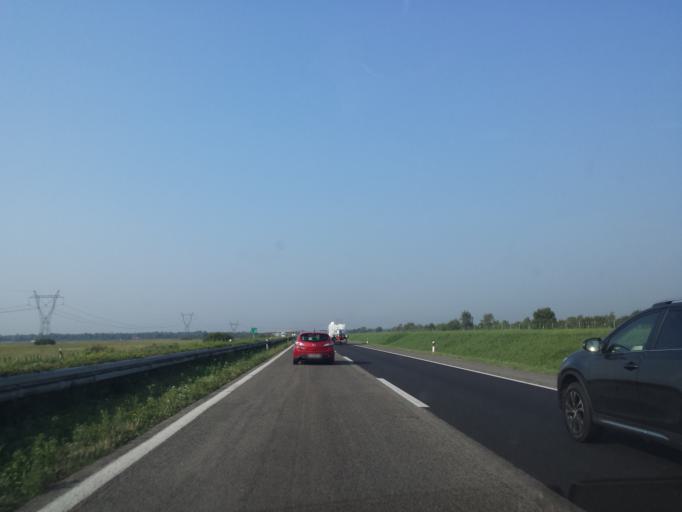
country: HR
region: Zagrebacka
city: Jastrebarsko
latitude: 45.6327
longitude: 15.6625
